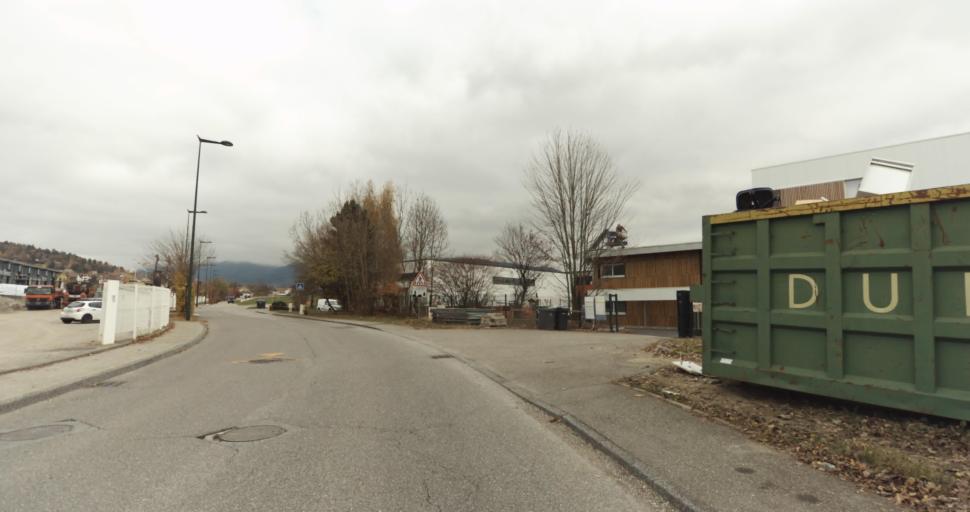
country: FR
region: Rhone-Alpes
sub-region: Departement de la Haute-Savoie
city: Pringy
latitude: 45.9408
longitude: 6.1283
